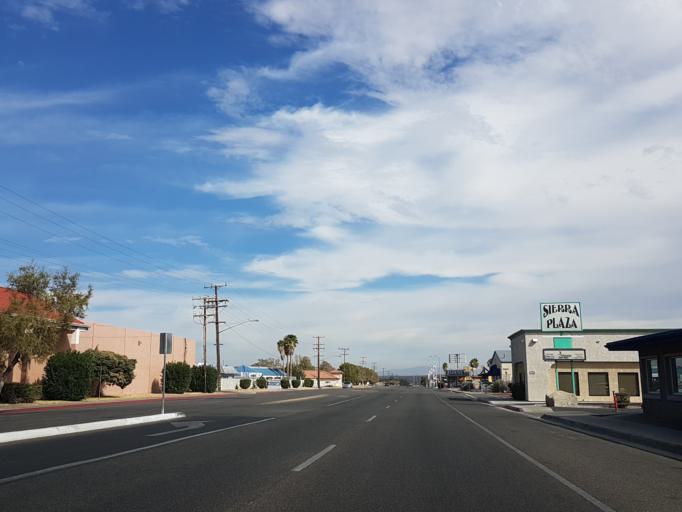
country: US
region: California
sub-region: Kern County
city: Ridgecrest
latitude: 35.6225
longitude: -117.6688
